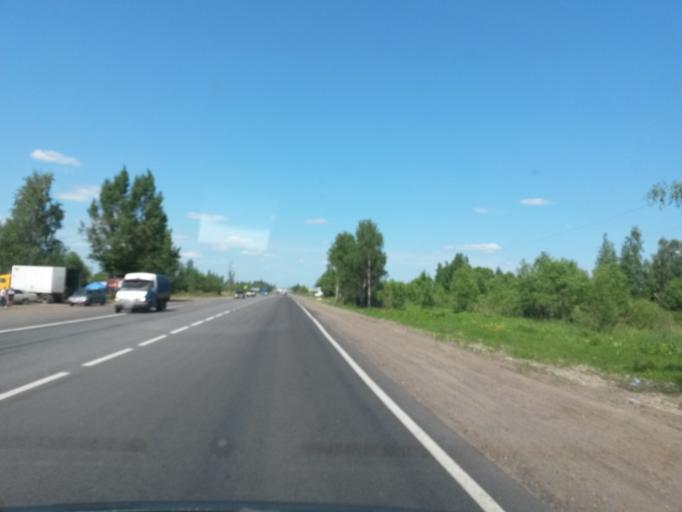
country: RU
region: Jaroslavl
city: Yaroslavl
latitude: 57.6054
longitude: 39.7933
